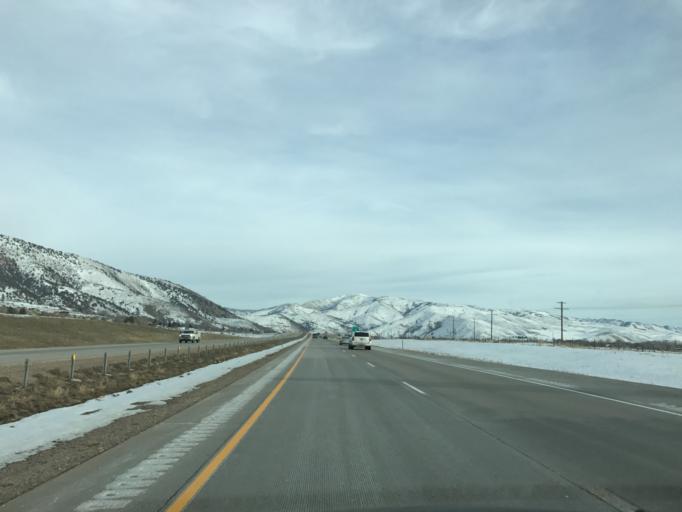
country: US
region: Utah
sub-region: Morgan County
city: Morgan
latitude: 41.0579
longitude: -111.6986
